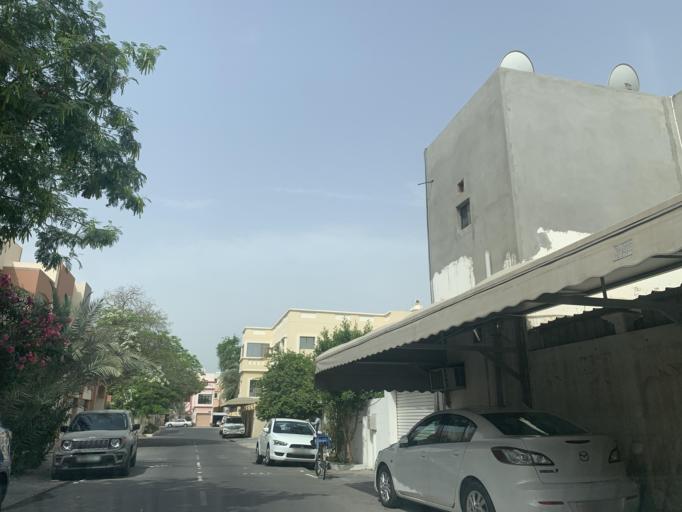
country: BH
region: Northern
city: Ar Rifa'
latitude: 26.1334
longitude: 50.5680
